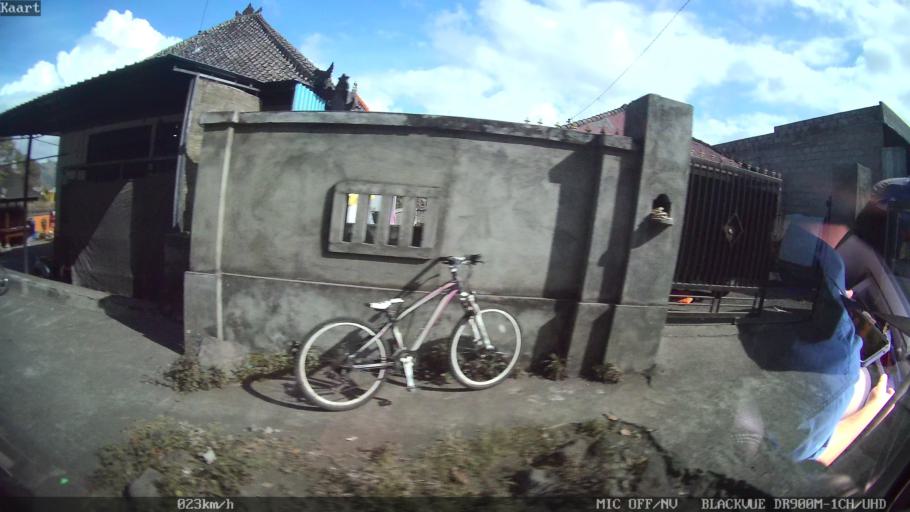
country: ID
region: Bali
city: Banjar Trunyan
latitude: -8.2264
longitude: 115.4057
